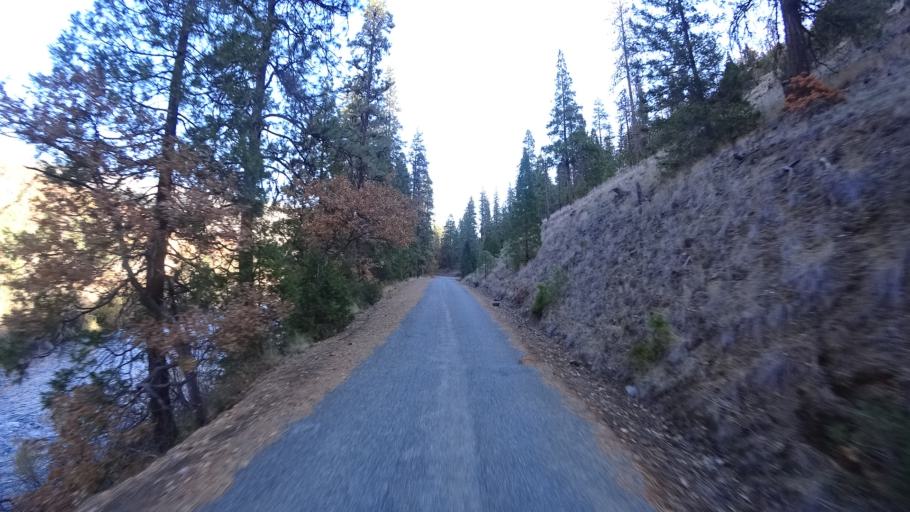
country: US
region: California
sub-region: Siskiyou County
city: Yreka
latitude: 41.8350
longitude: -122.9429
